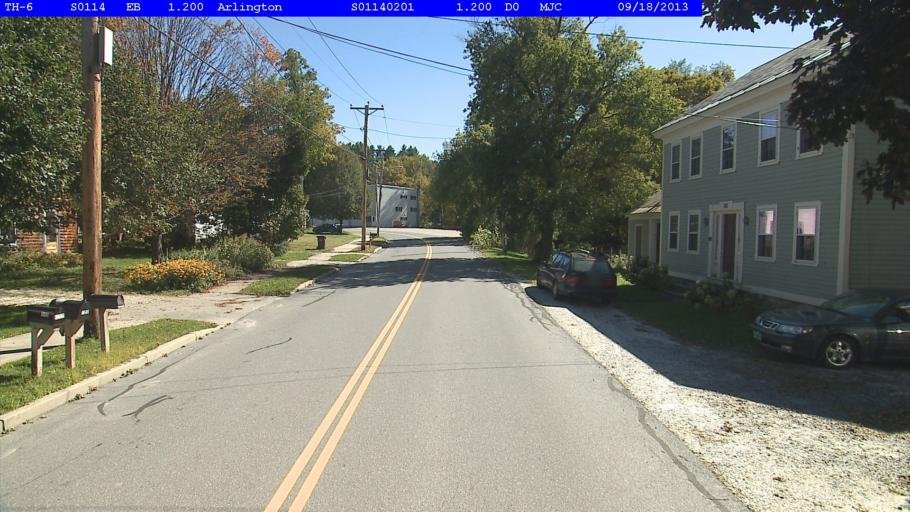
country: US
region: Vermont
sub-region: Bennington County
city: Arlington
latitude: 43.0613
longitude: -73.1426
